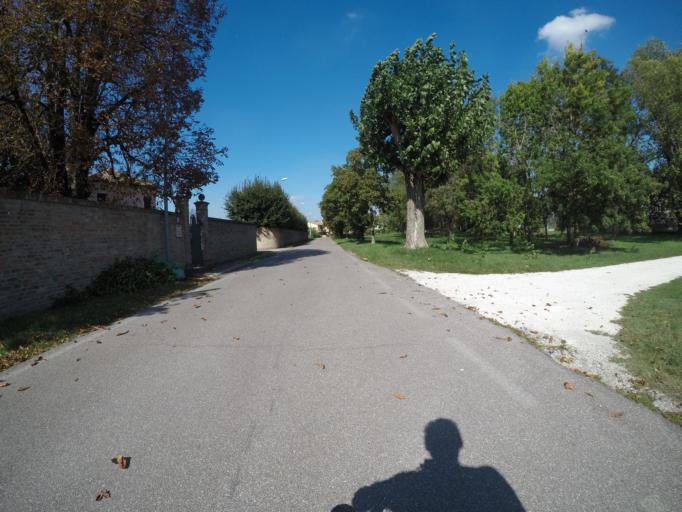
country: IT
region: Veneto
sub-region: Provincia di Rovigo
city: Polesella
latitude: 44.9648
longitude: 11.7488
